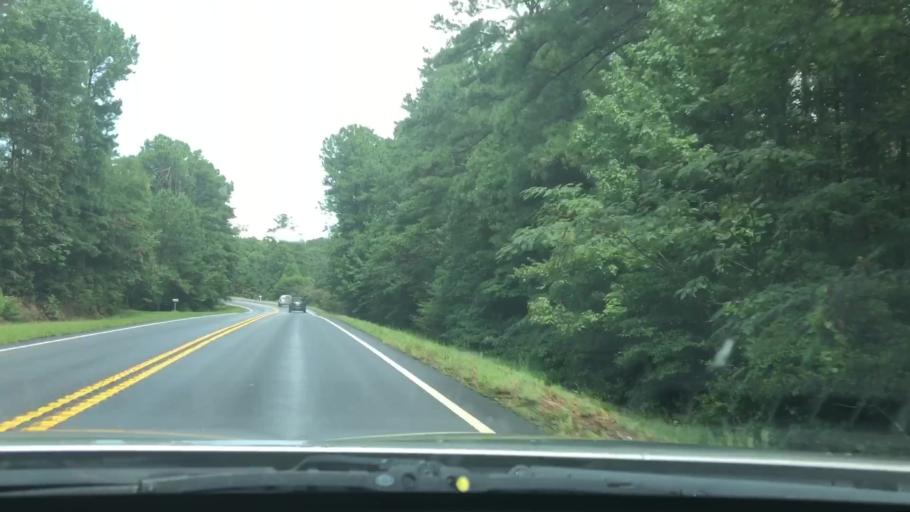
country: US
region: Georgia
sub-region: Lamar County
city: Barnesville
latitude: 33.0921
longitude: -84.1531
